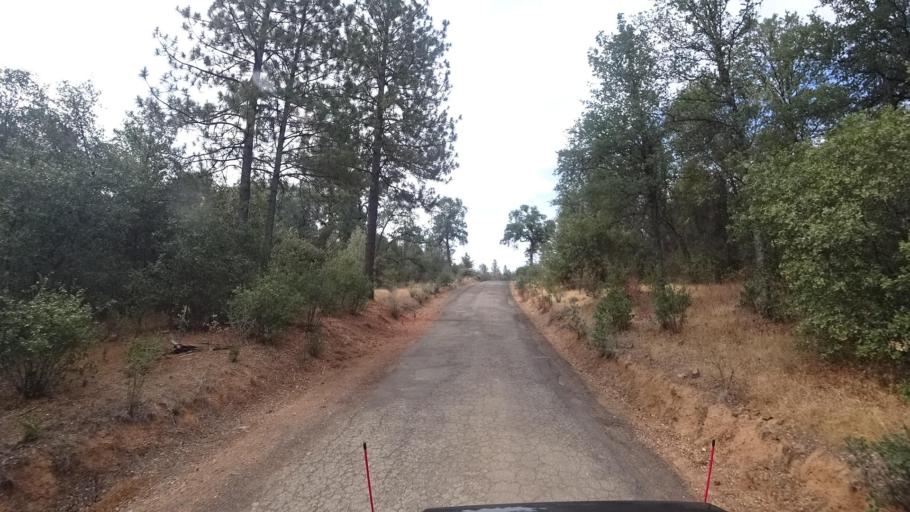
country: US
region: California
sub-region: Mariposa County
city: Midpines
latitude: 37.5176
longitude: -119.9368
